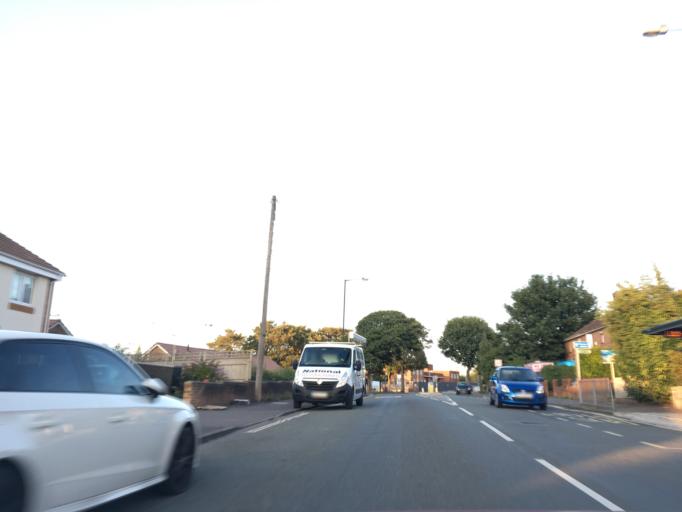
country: GB
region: England
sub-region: South Gloucestershire
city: Kingswood
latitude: 51.4666
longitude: -2.5329
